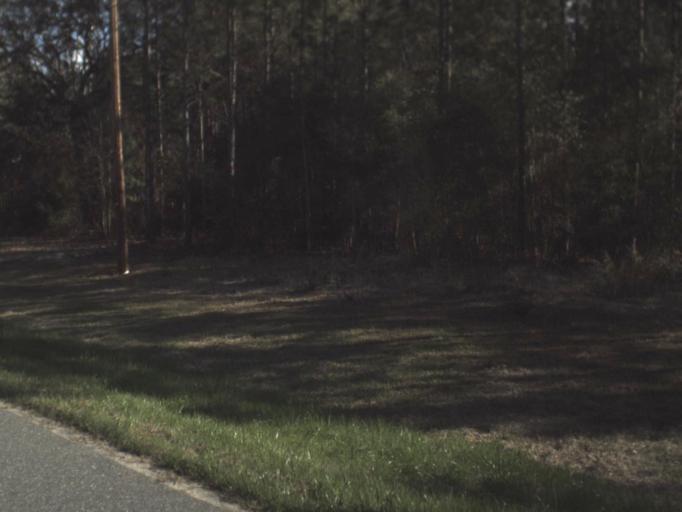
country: US
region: Florida
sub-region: Jackson County
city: Malone
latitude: 30.9161
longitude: -85.1607
